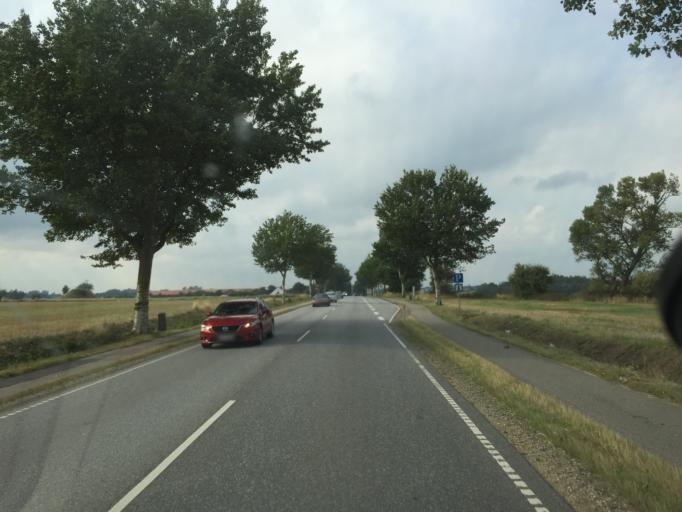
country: DK
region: Zealand
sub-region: Solrod Kommune
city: Havdrup
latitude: 55.5633
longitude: 12.1328
